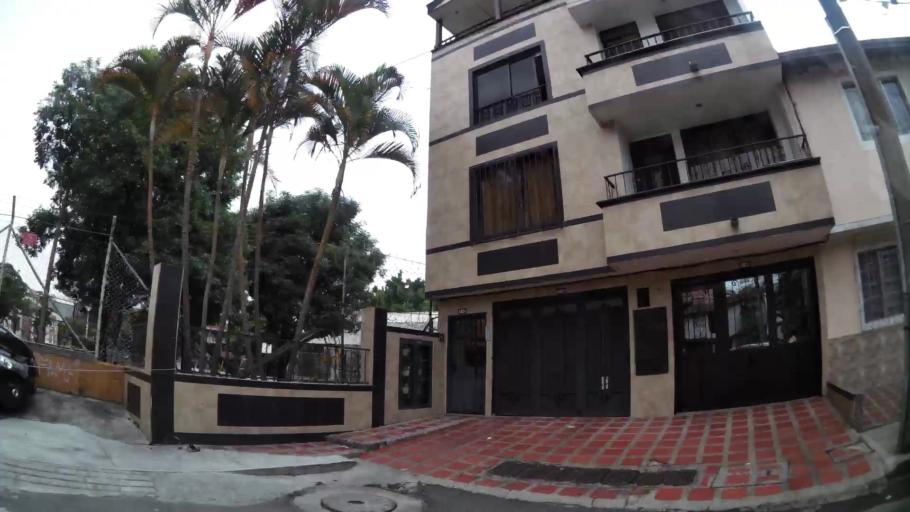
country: CO
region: Antioquia
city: Itagui
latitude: 6.2145
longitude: -75.5858
